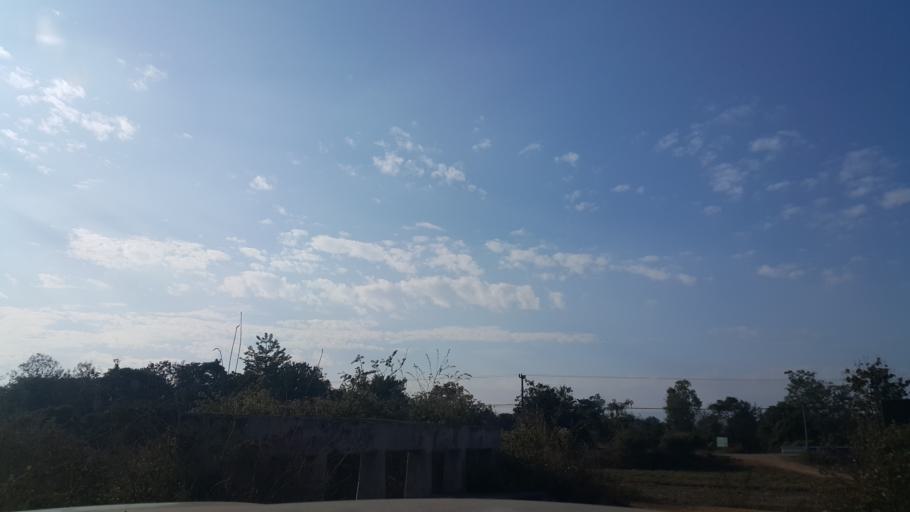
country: TH
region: Lampang
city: Ko Kha
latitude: 18.2258
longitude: 99.3524
